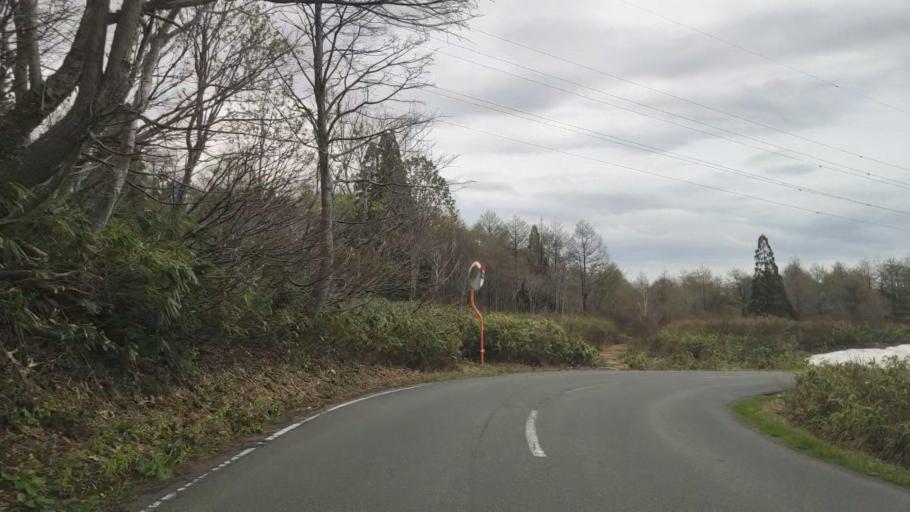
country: JP
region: Aomori
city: Aomori Shi
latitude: 40.7142
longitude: 140.8731
